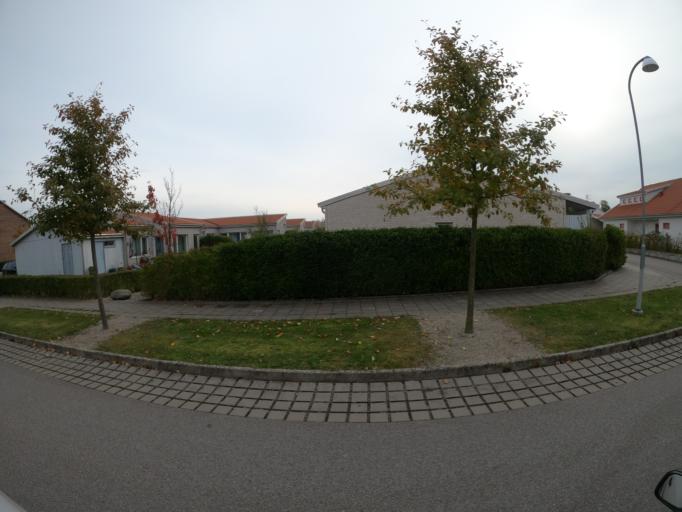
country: SE
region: Skane
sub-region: Lunds Kommun
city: Lund
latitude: 55.7494
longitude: 13.1889
